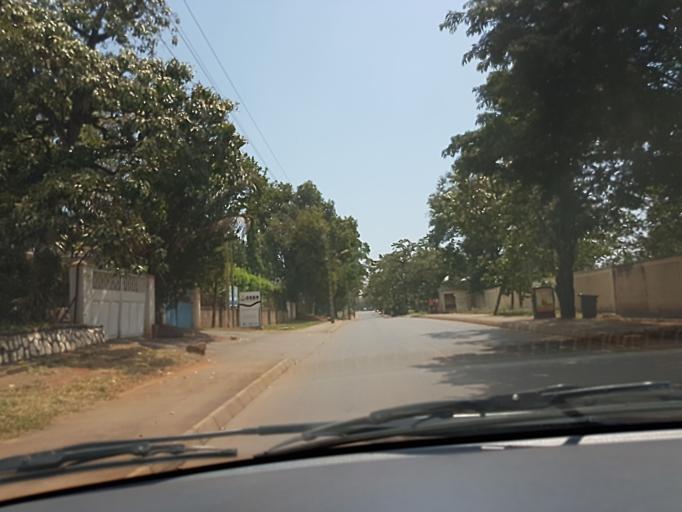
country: UG
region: Central Region
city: Kampala Central Division
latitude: 0.3283
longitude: 32.5768
